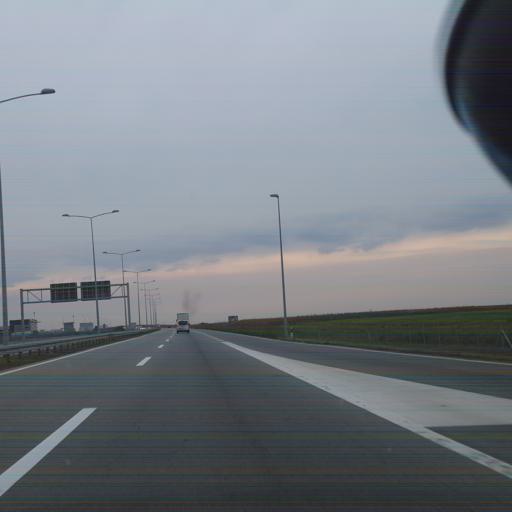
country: RS
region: Autonomna Pokrajina Vojvodina
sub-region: Juznobacki Okrug
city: Kovilj
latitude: 45.2441
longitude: 20.0322
